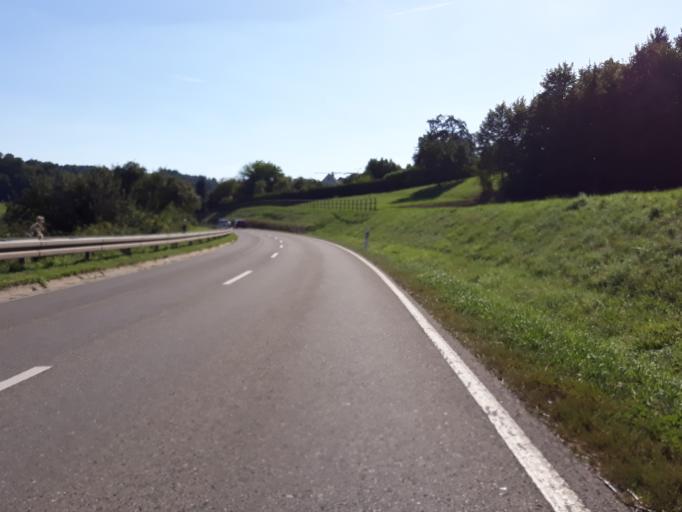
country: DE
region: Baden-Wuerttemberg
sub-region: Karlsruhe Region
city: Gechingen
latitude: 48.6989
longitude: 8.8385
